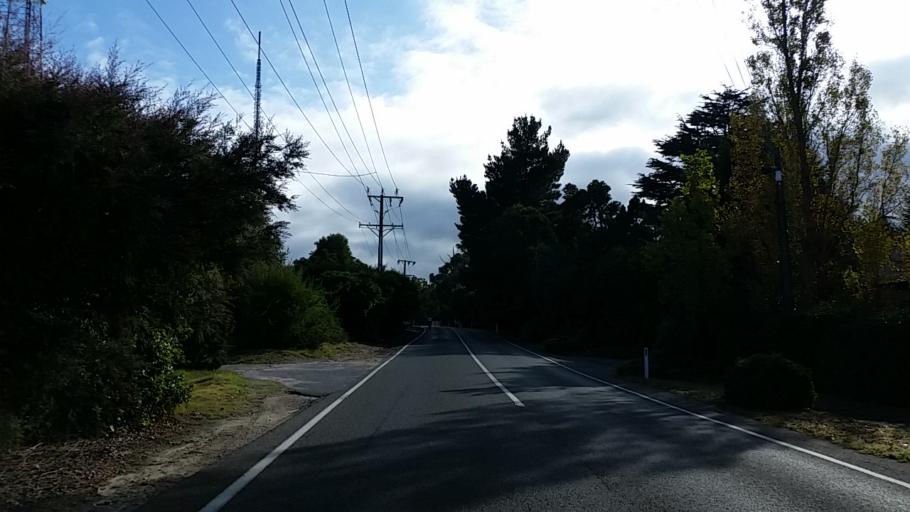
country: AU
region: South Australia
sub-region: Adelaide Hills
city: Crafers
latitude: -34.9826
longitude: 138.7087
